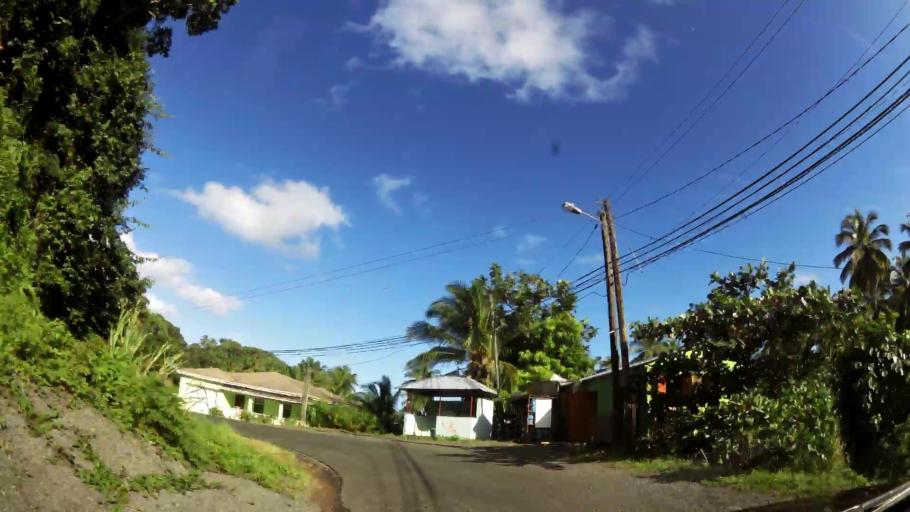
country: DM
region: Saint Andrew
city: Calibishie
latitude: 15.5924
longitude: -61.3824
